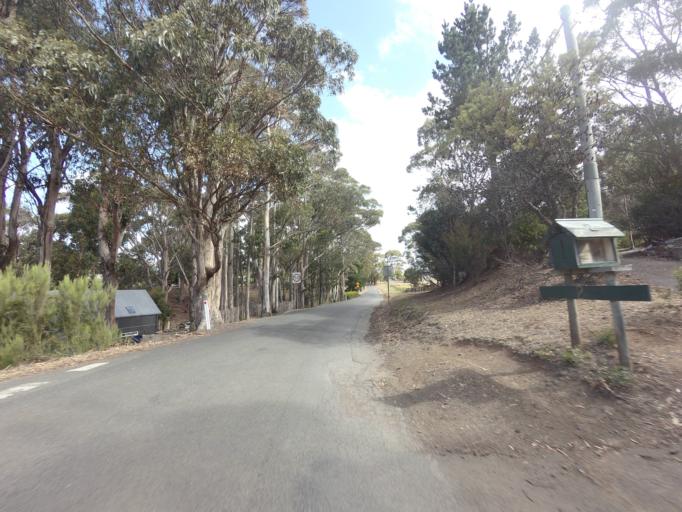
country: AU
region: Tasmania
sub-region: Hobart
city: Dynnyrne
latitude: -42.9238
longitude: 147.2878
